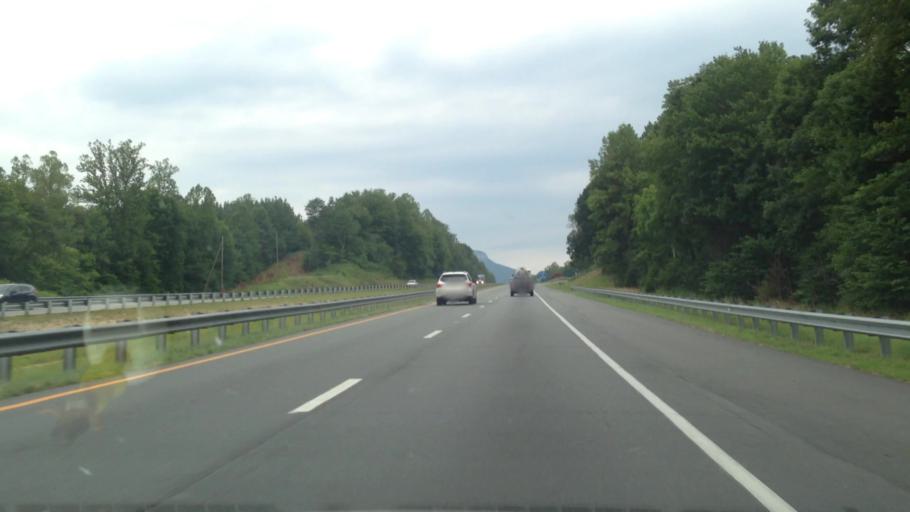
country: US
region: North Carolina
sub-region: Stokes County
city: King
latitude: 36.3032
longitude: -80.4171
